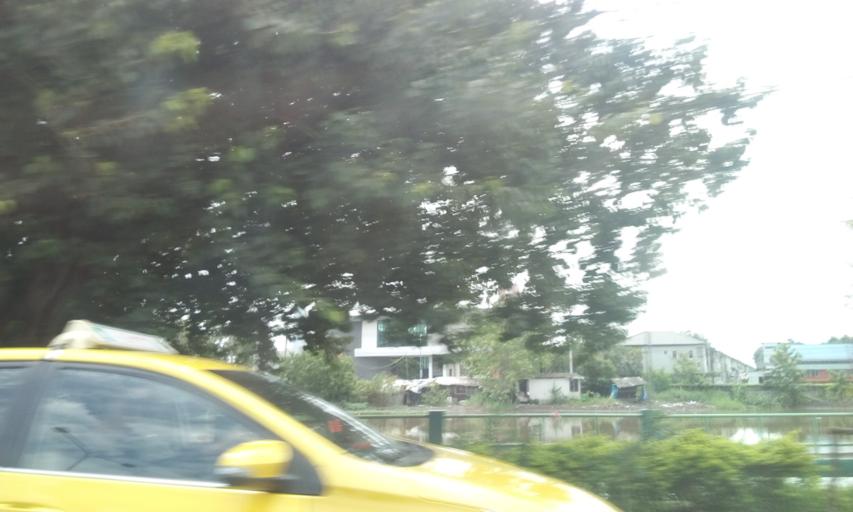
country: TH
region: Pathum Thani
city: Thanyaburi
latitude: 14.0042
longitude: 100.6961
